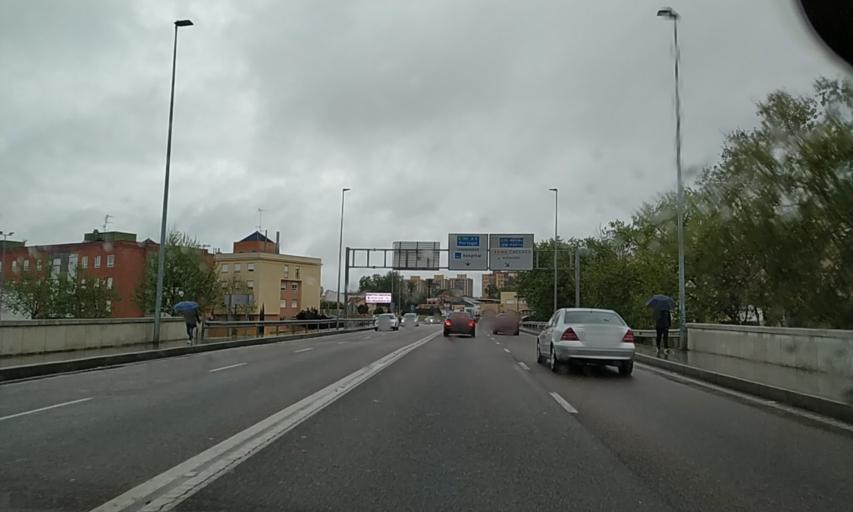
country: ES
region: Extremadura
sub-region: Provincia de Badajoz
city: Badajoz
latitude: 38.8826
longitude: -6.9842
